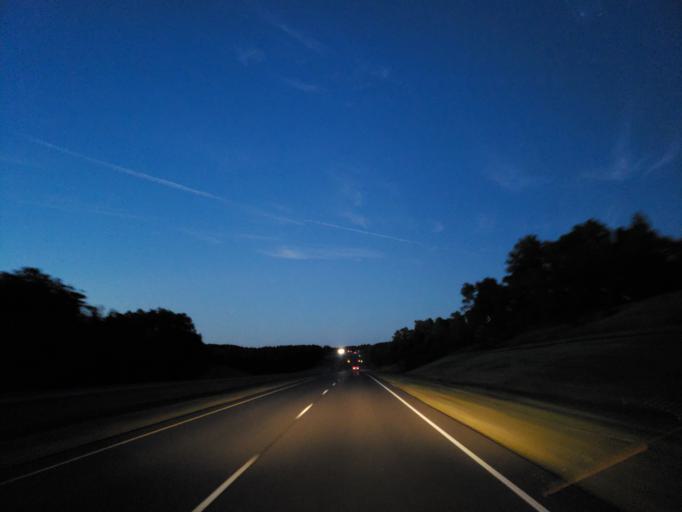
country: US
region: Mississippi
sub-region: Clarke County
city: Quitman
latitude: 32.0295
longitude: -88.6820
